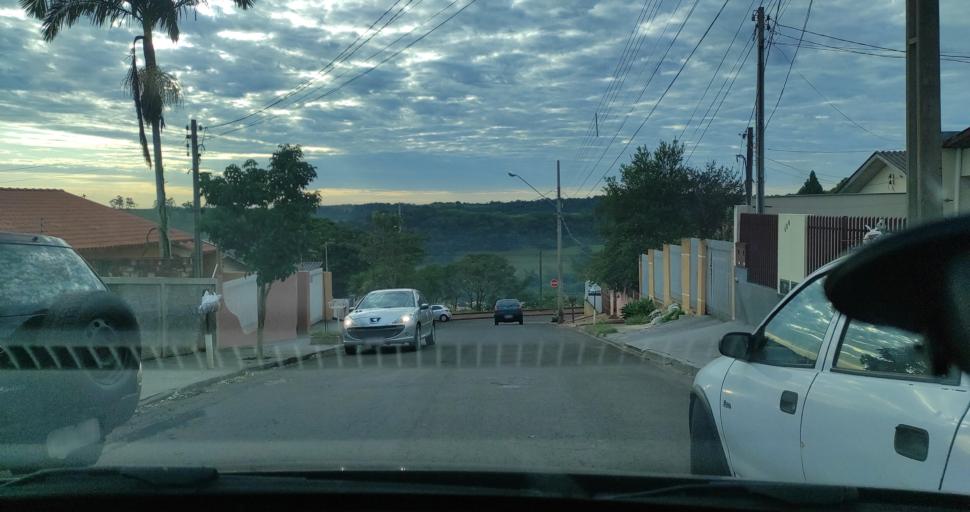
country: BR
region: Parana
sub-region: Ibipora
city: Ibipora
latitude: -23.2541
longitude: -51.0492
